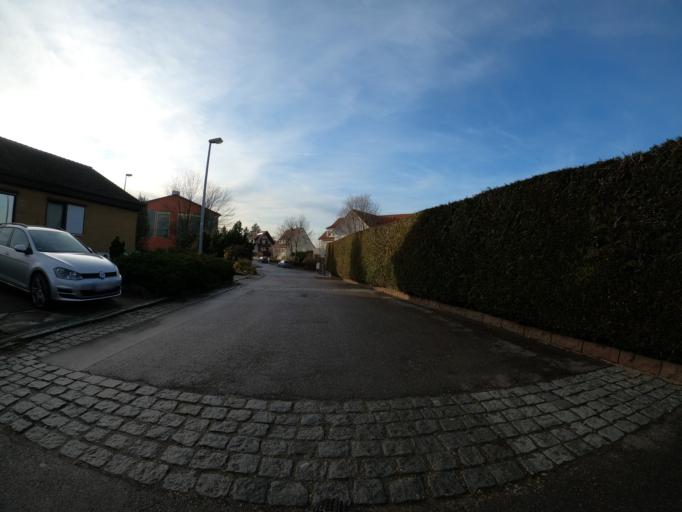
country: DE
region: Baden-Wuerttemberg
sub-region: Regierungsbezirk Stuttgart
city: Boll
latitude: 48.6462
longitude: 9.6207
